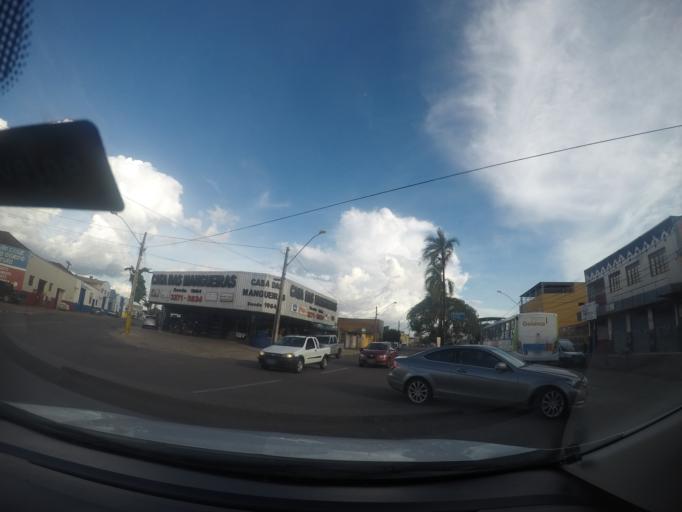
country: BR
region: Goias
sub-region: Goiania
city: Goiania
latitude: -16.6689
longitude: -49.3066
